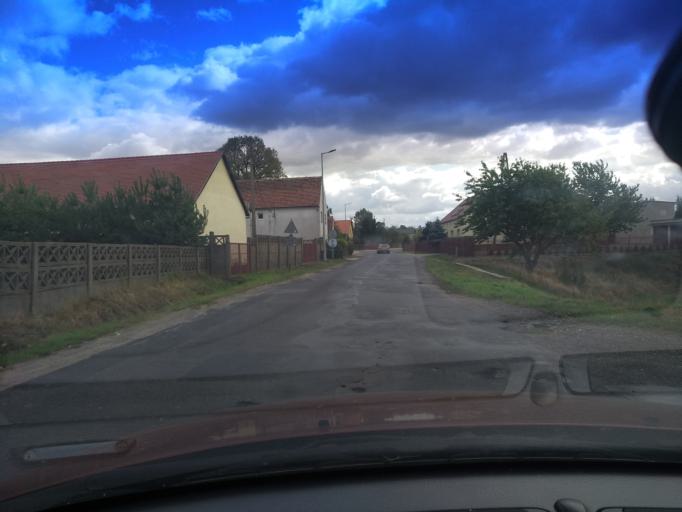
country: PL
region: Lower Silesian Voivodeship
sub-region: Powiat zgorzelecki
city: Zgorzelec
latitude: 51.1897
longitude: 15.0107
